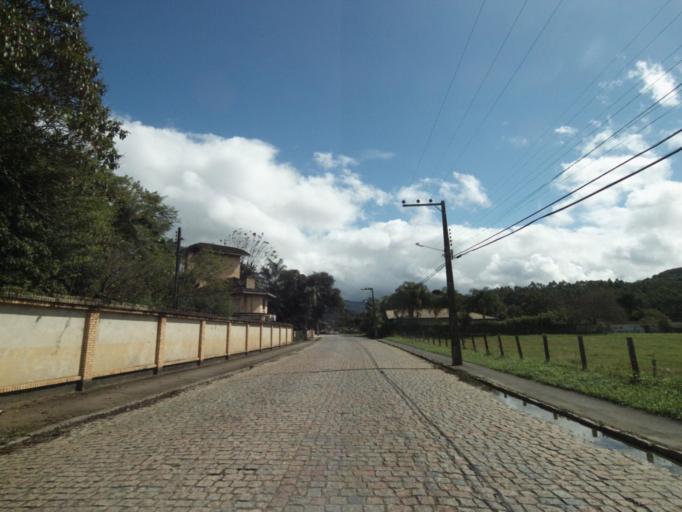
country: BR
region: Santa Catarina
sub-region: Pomerode
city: Pomerode
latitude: -26.7054
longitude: -49.1662
